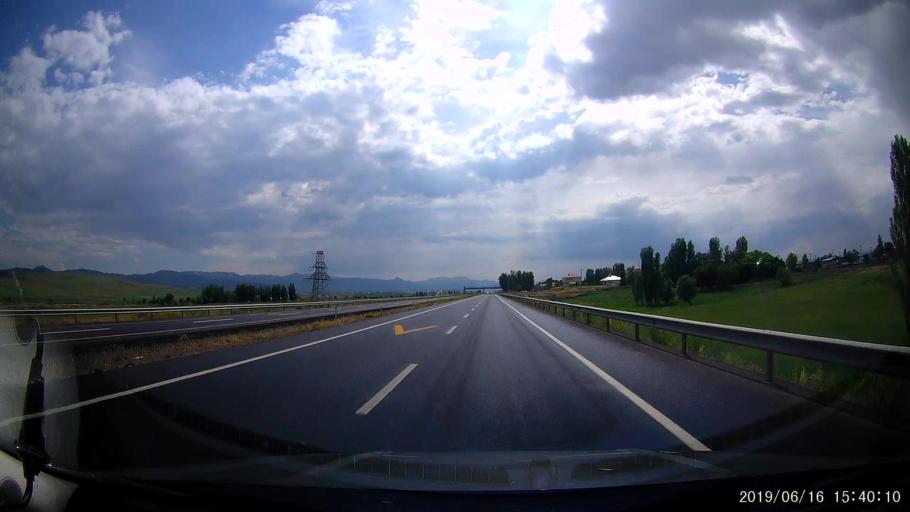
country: TR
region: Erzurum
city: Koprukoy
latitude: 39.9684
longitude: 41.8782
